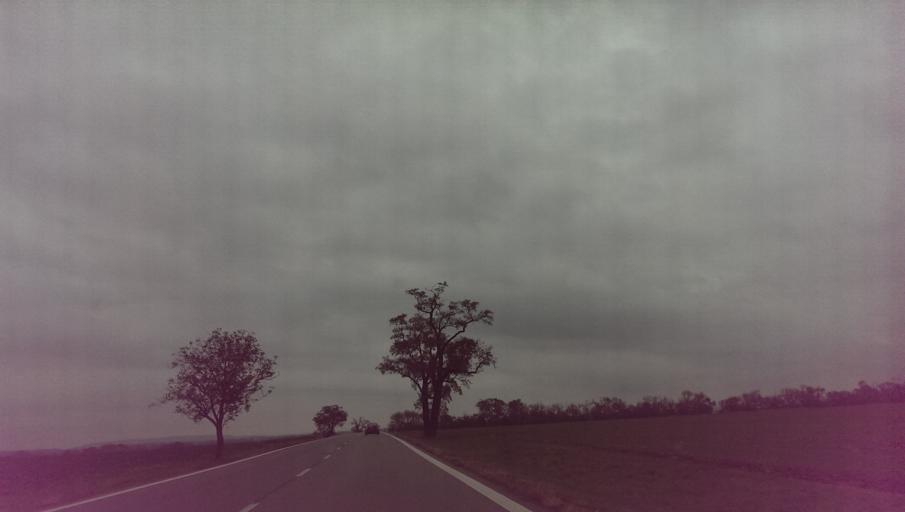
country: CZ
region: South Moravian
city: Pohorelice
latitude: 48.9718
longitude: 16.4770
